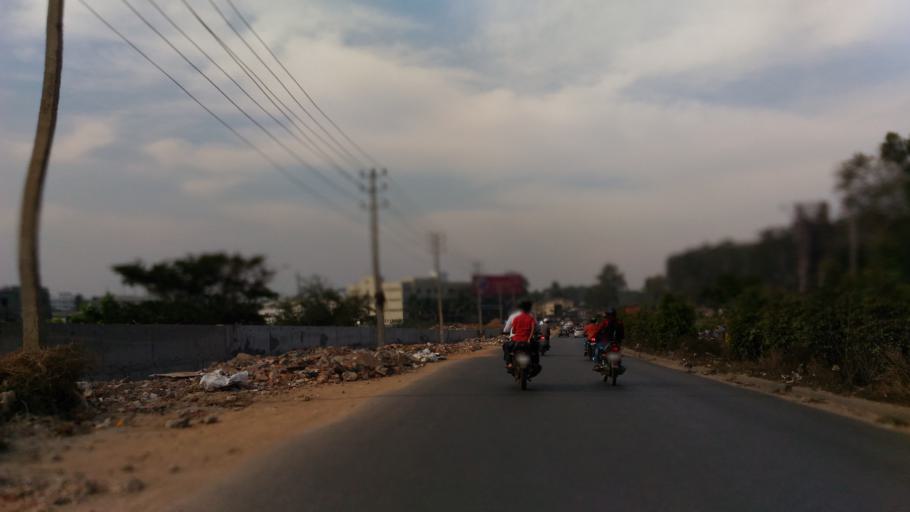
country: IN
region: Karnataka
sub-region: Bangalore Urban
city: Bangalore
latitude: 12.9326
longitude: 77.5085
